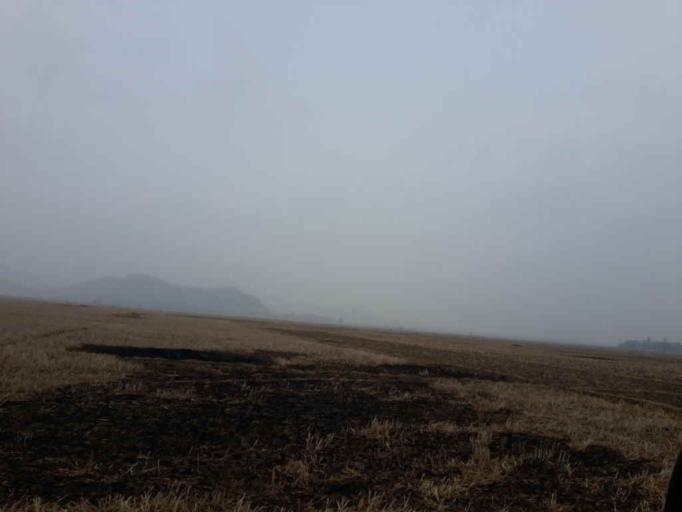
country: IN
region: Manipur
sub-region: Imphal East
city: Imphal
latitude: 24.8668
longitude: 93.9994
